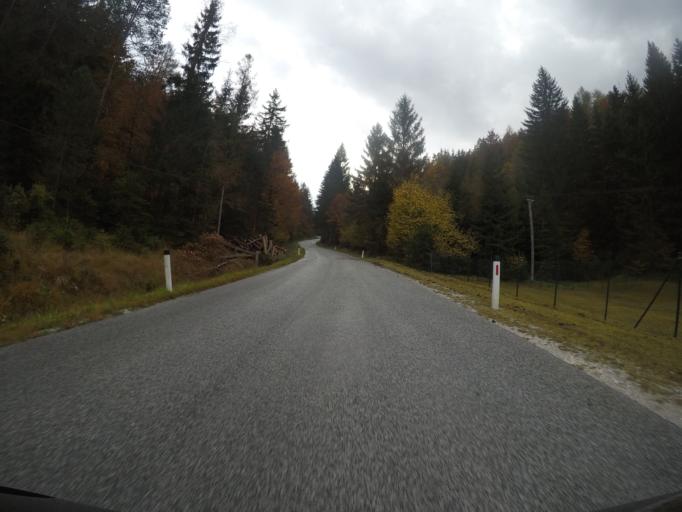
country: SI
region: Kranjska Gora
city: Mojstrana
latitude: 46.4471
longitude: 13.9326
